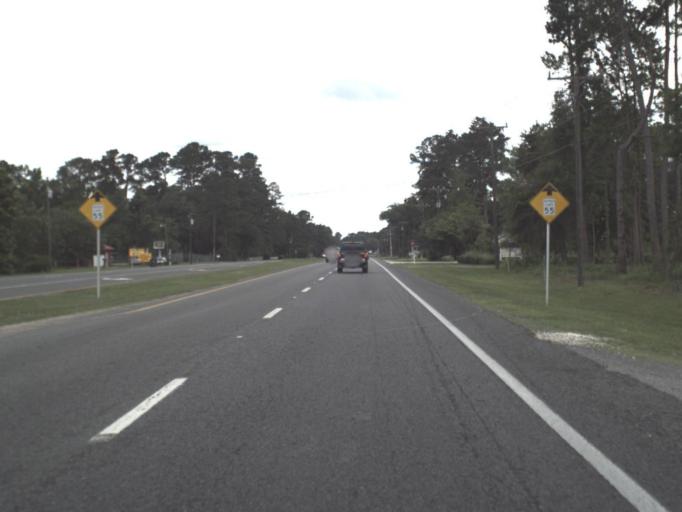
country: US
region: Florida
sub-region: Nassau County
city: Callahan
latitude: 30.5479
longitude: -81.8183
